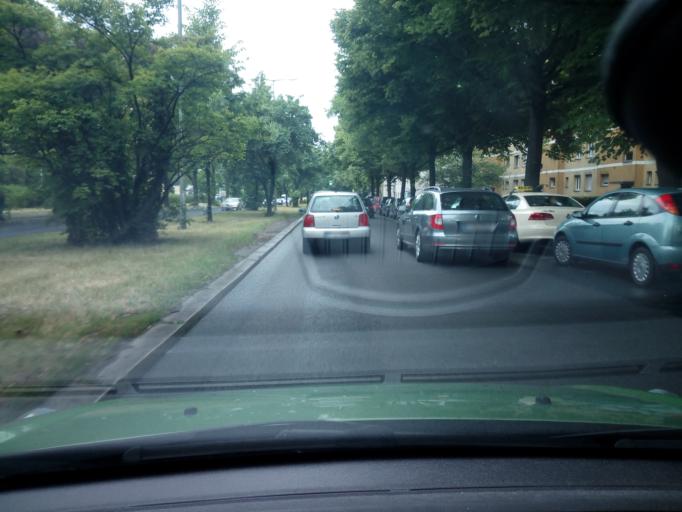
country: DE
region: Berlin
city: Tempelhof Bezirk
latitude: 52.4799
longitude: 13.3856
